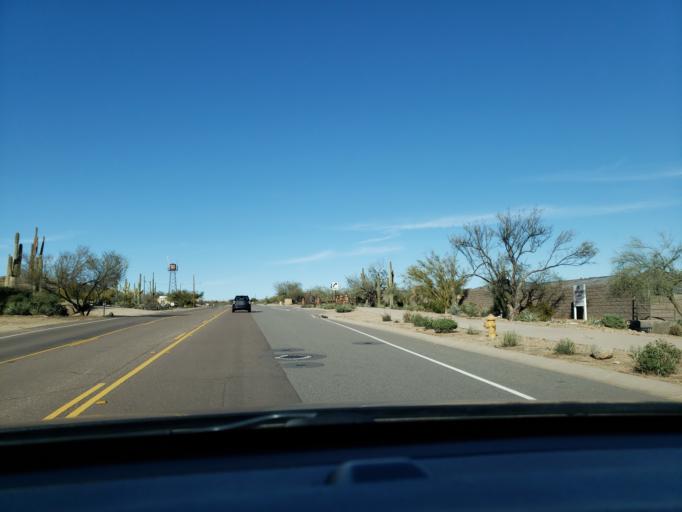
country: US
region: Arizona
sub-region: Maricopa County
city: Carefree
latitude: 33.7320
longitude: -111.8487
